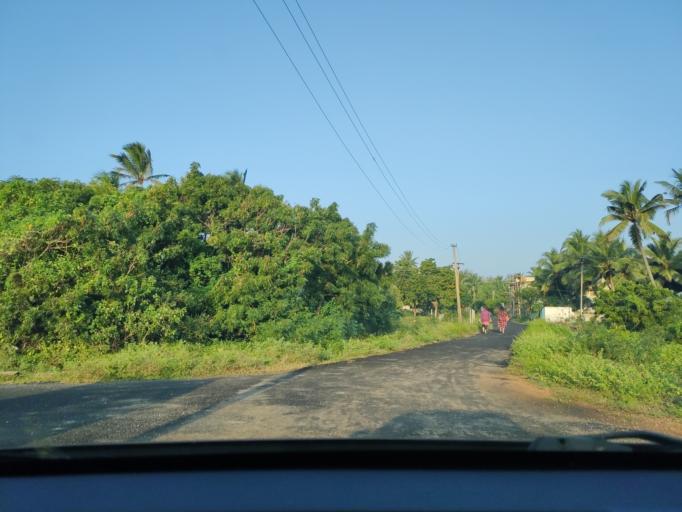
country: IN
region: Tamil Nadu
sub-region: Villupuram
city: Auroville
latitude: 12.0636
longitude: 79.8836
